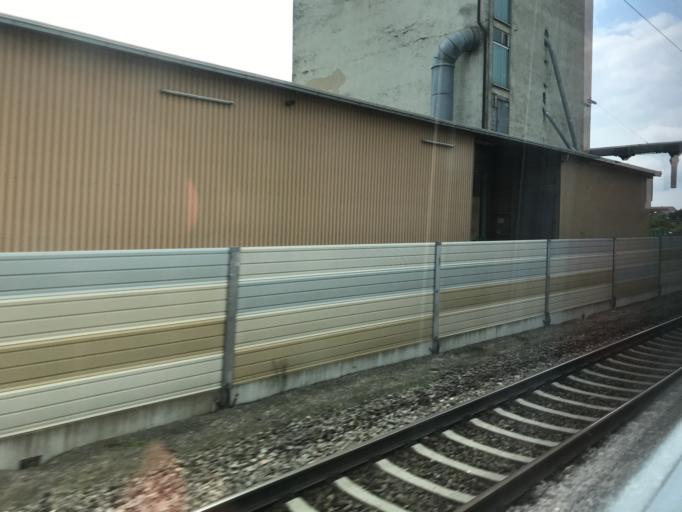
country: DE
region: Baden-Wuerttemberg
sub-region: Tuebingen Region
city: Beimerstetten
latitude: 48.4844
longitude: 9.9771
